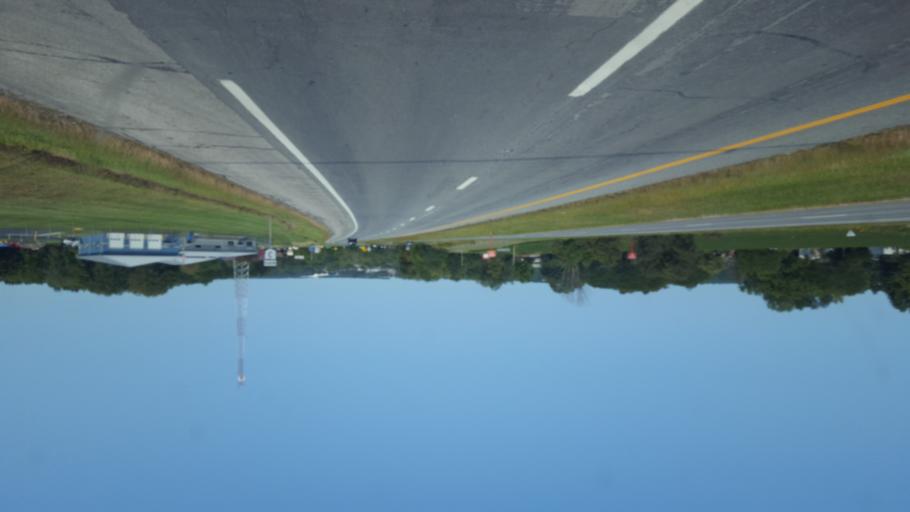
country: US
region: Ohio
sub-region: Wayne County
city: Wooster
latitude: 40.7849
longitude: -81.9636
